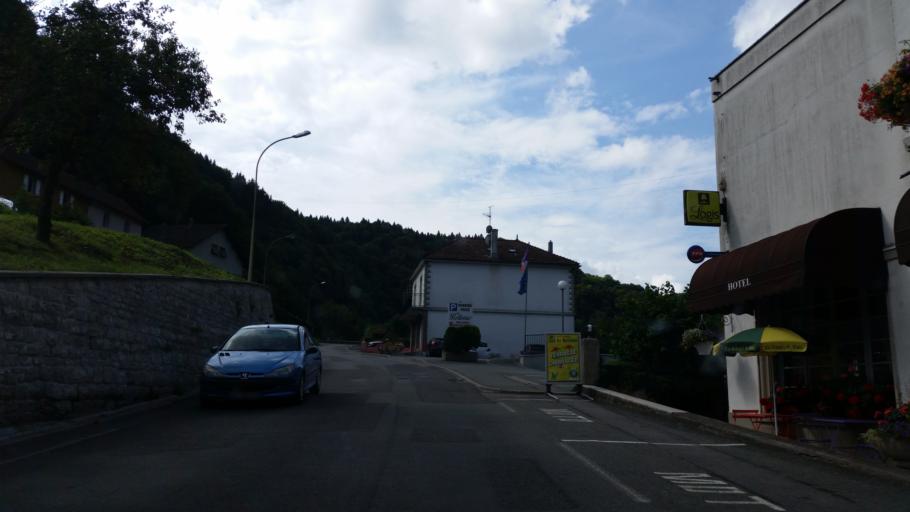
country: FR
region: Franche-Comte
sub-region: Departement du Doubs
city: Saint-Hippolyte
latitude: 47.3162
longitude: 6.8115
